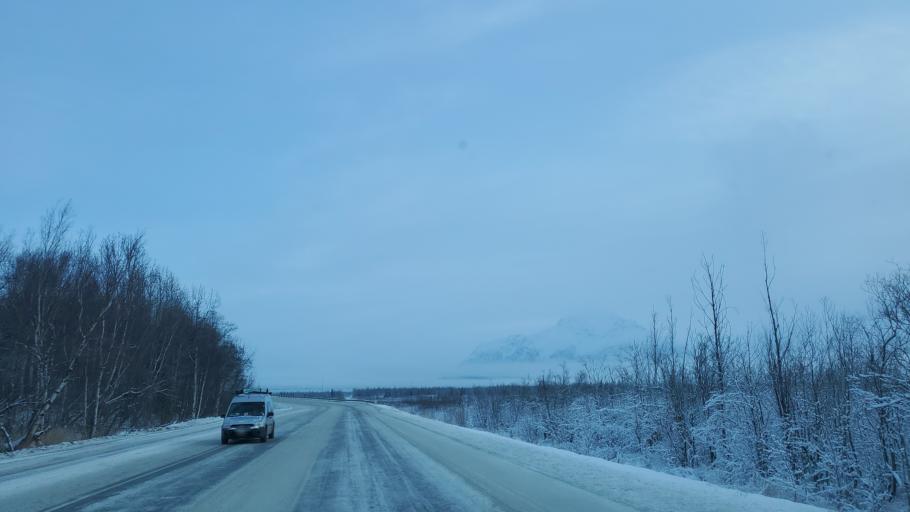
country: US
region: Alaska
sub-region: Matanuska-Susitna Borough
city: Gateway
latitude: 61.5502
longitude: -149.2870
